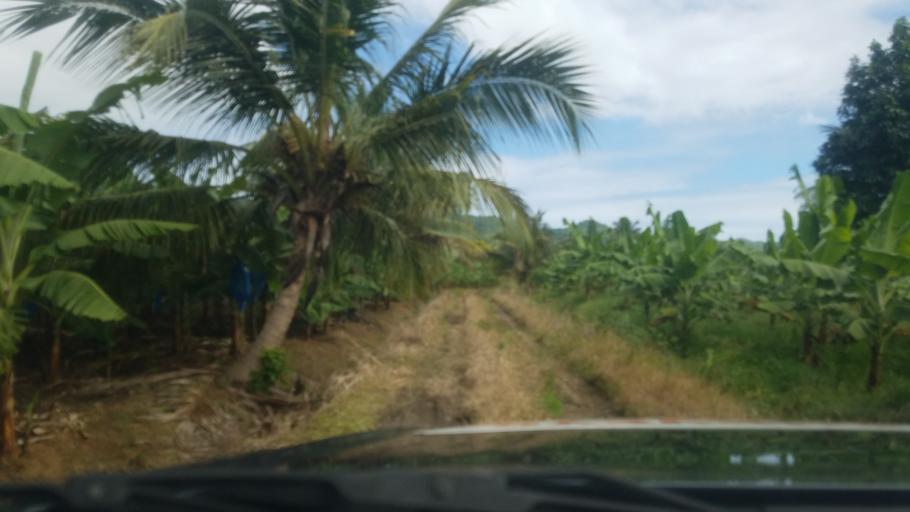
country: LC
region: Dennery Quarter
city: Dennery
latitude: 13.9339
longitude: -60.9201
